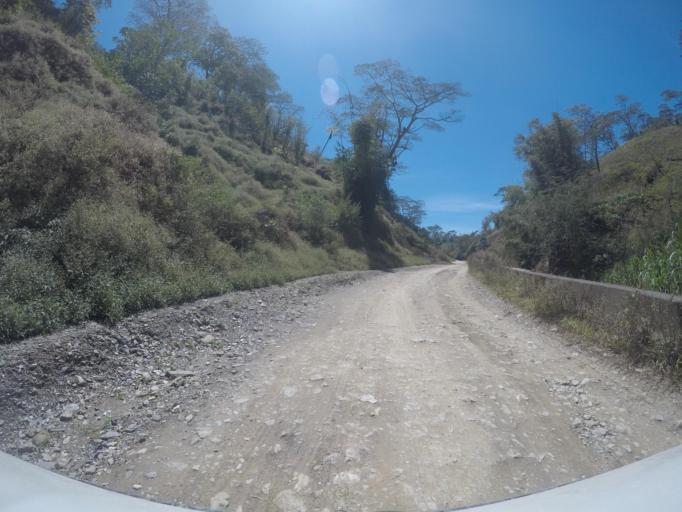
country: TL
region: Ermera
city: Gleno
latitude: -8.7766
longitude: 125.3842
